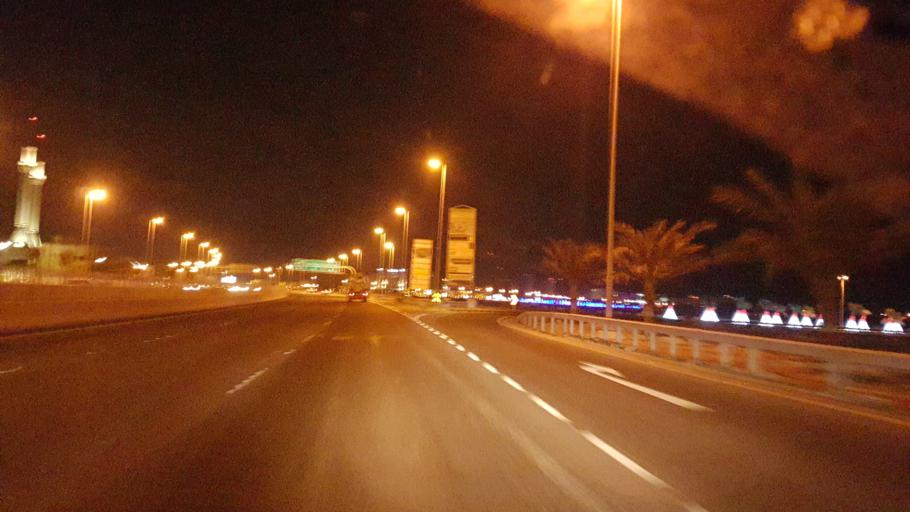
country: BH
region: Muharraq
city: Al Hadd
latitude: 26.2693
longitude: 50.6620
